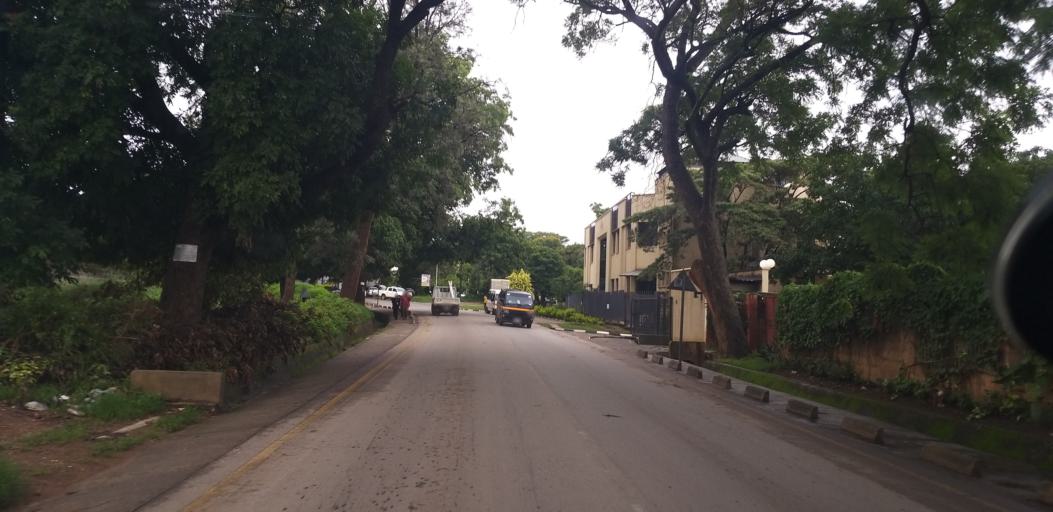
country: ZM
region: Lusaka
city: Lusaka
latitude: -15.4198
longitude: 28.2987
